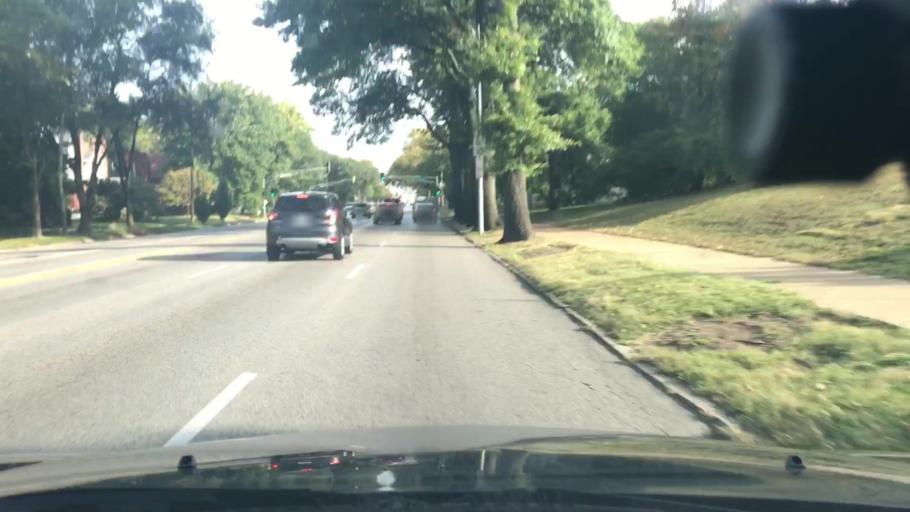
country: US
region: Missouri
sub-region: Saint Louis County
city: Richmond Heights
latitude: 38.6088
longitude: -90.2684
